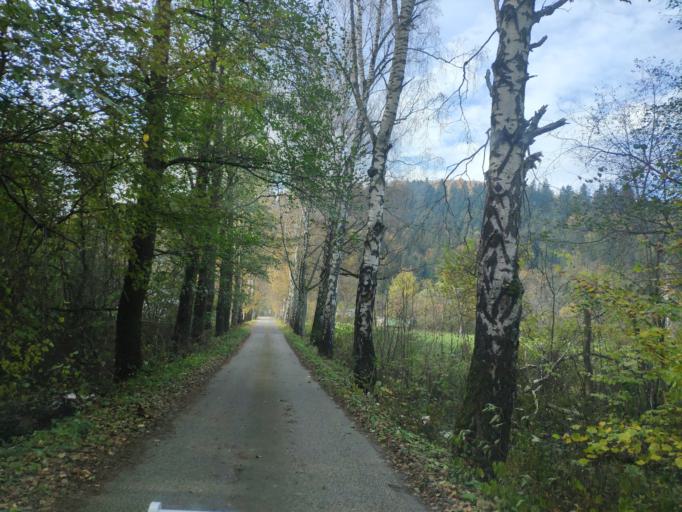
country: SK
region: Kosicky
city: Spisska Nova Ves
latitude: 48.8114
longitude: 20.6884
